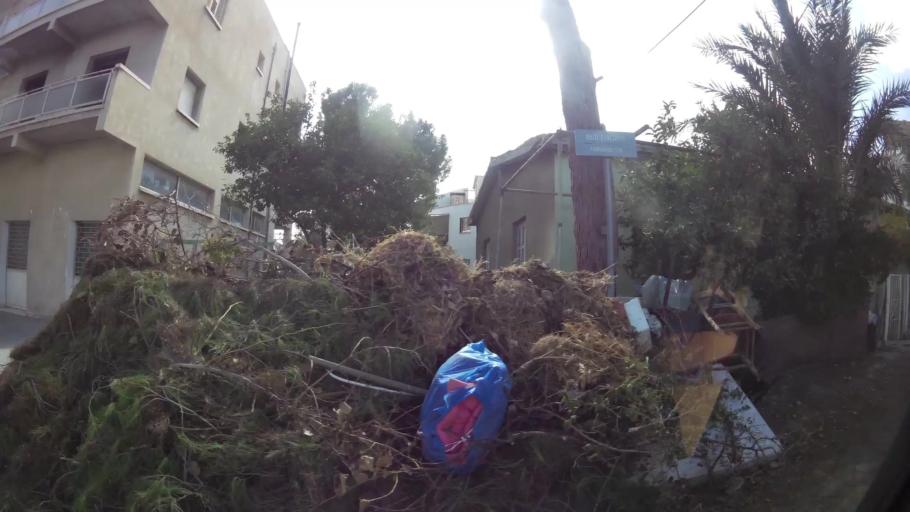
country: CY
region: Lefkosia
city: Nicosia
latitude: 35.1833
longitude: 33.3861
